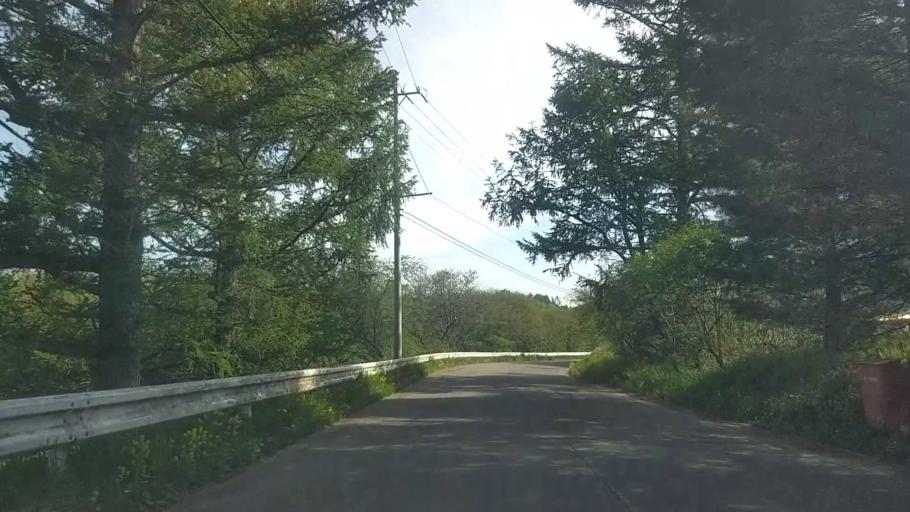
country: JP
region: Yamanashi
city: Nirasaki
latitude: 35.9380
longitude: 138.4765
